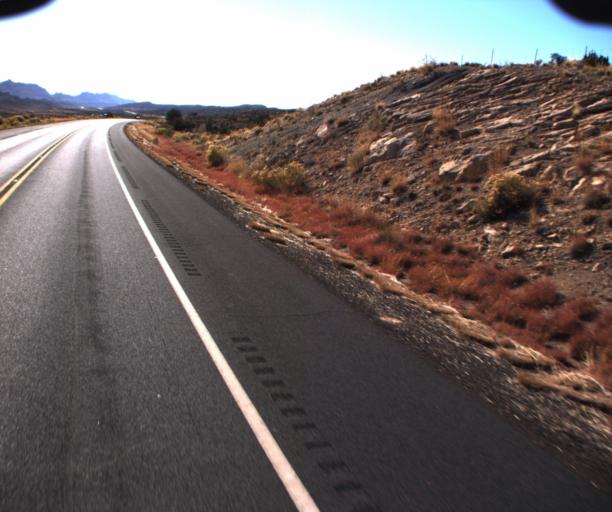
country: US
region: Arizona
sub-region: Coconino County
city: Tuba City
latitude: 36.3430
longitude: -111.4996
